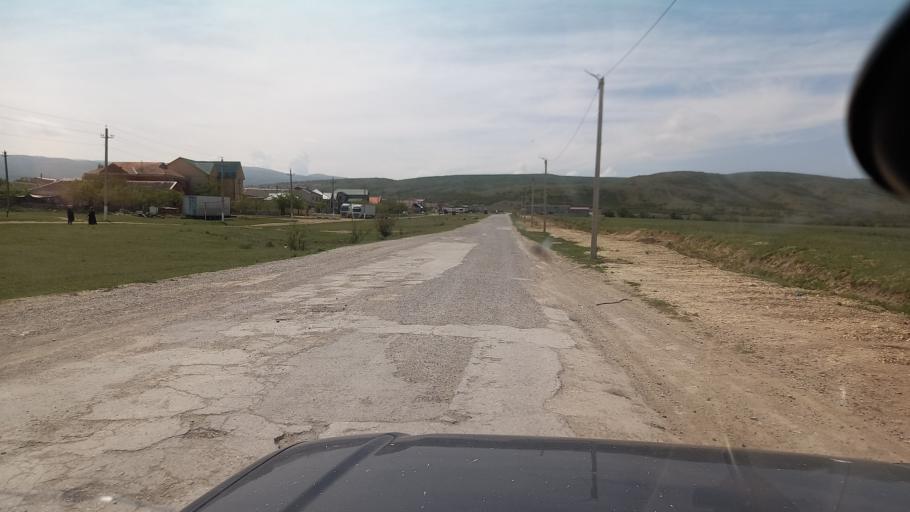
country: RU
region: Dagestan
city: Gurbuki
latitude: 42.6173
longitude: 47.5915
